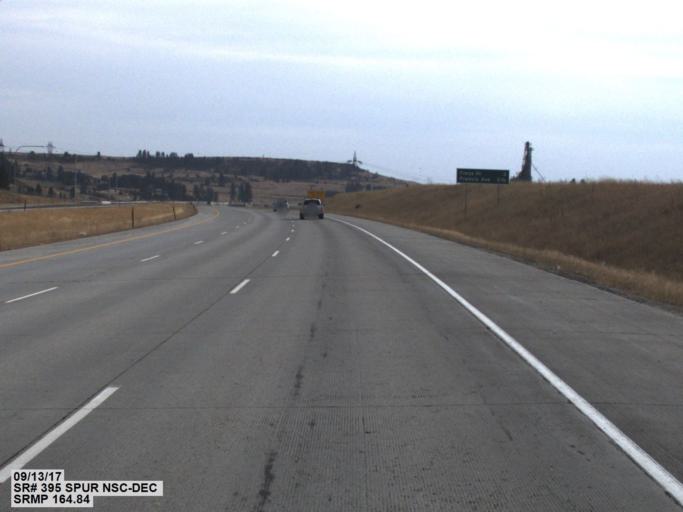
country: US
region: Washington
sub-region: Spokane County
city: Mead
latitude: 47.7607
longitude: -117.3663
